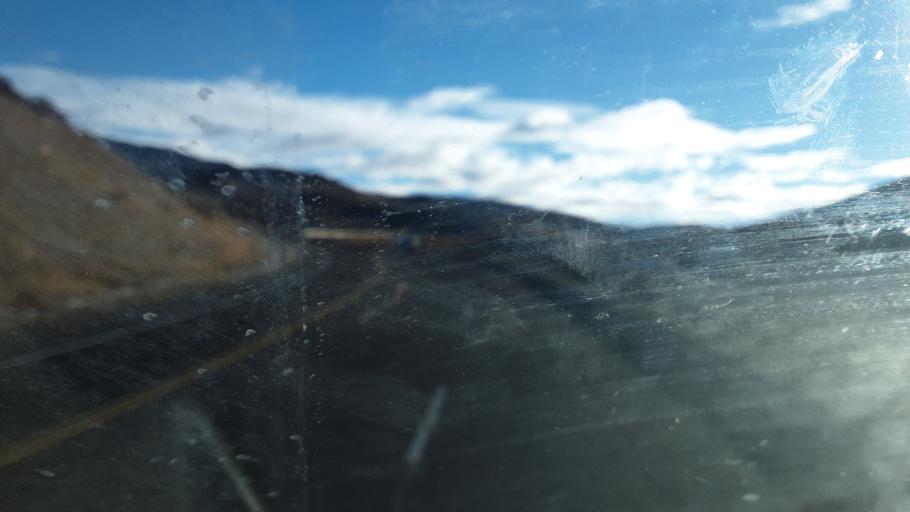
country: US
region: Colorado
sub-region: Montrose County
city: Montrose
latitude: 38.4516
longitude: -107.6595
